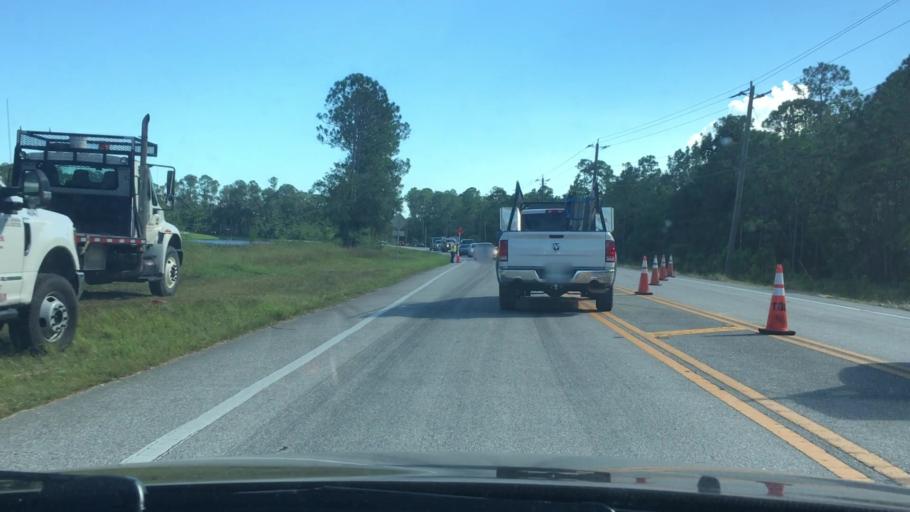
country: US
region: Florida
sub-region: Volusia County
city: Samsula-Spruce Creek
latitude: 29.1097
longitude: -81.0698
